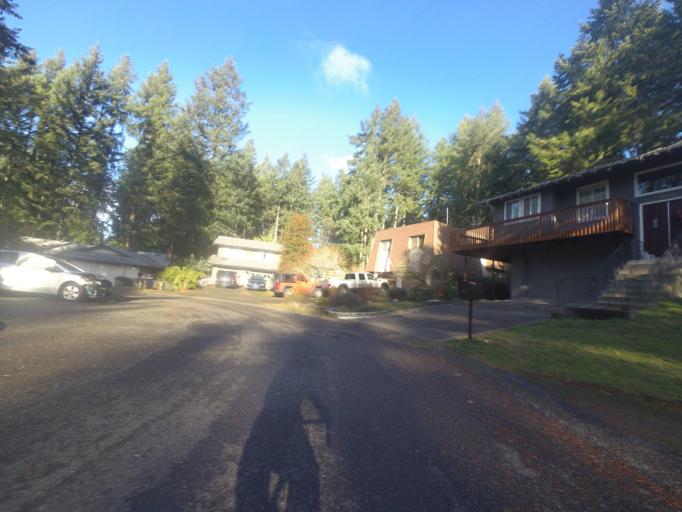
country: US
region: Washington
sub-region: Pierce County
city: University Place
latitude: 47.2110
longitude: -122.5618
